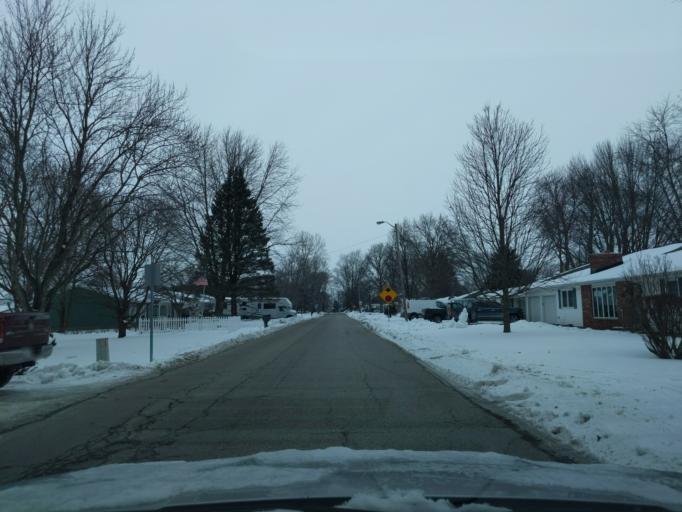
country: US
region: Indiana
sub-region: Benton County
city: Otterbein
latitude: 40.4827
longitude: -87.0946
